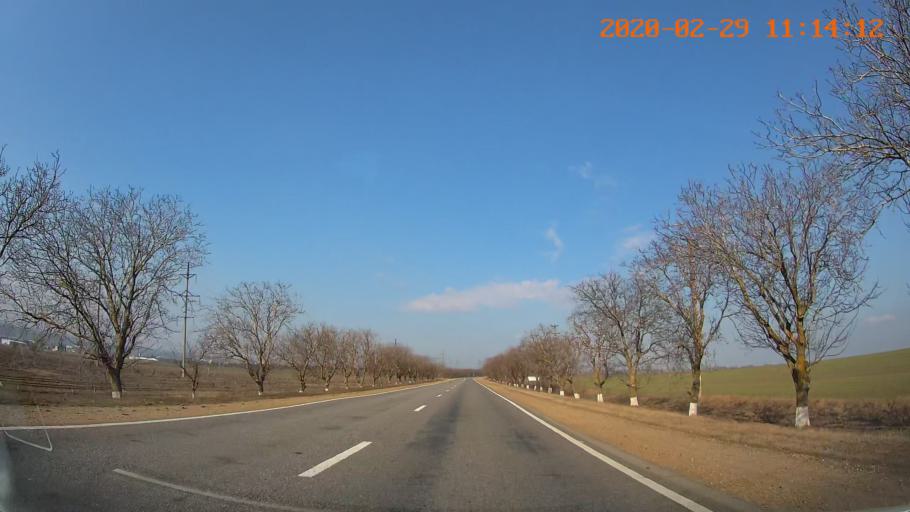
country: MD
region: Telenesti
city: Dubasari
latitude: 47.2798
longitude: 29.1747
